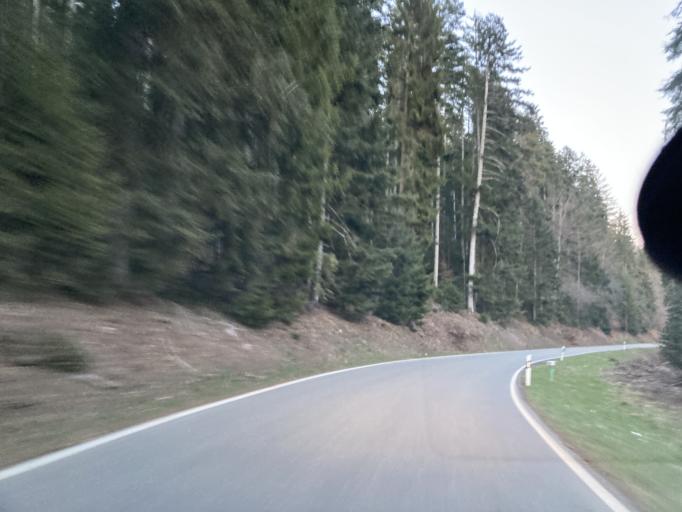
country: DE
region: Baden-Wuerttemberg
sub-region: Karlsruhe Region
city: Neuweiler
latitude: 48.6801
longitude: 8.6363
